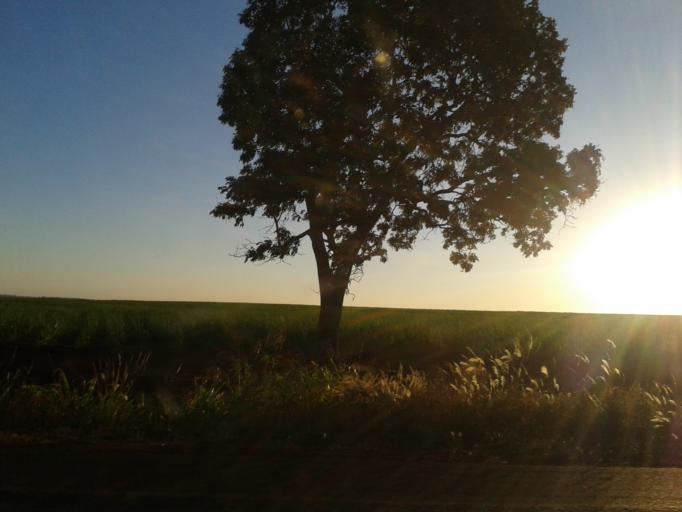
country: BR
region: Minas Gerais
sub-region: Centralina
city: Centralina
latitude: -18.7164
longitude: -49.2789
